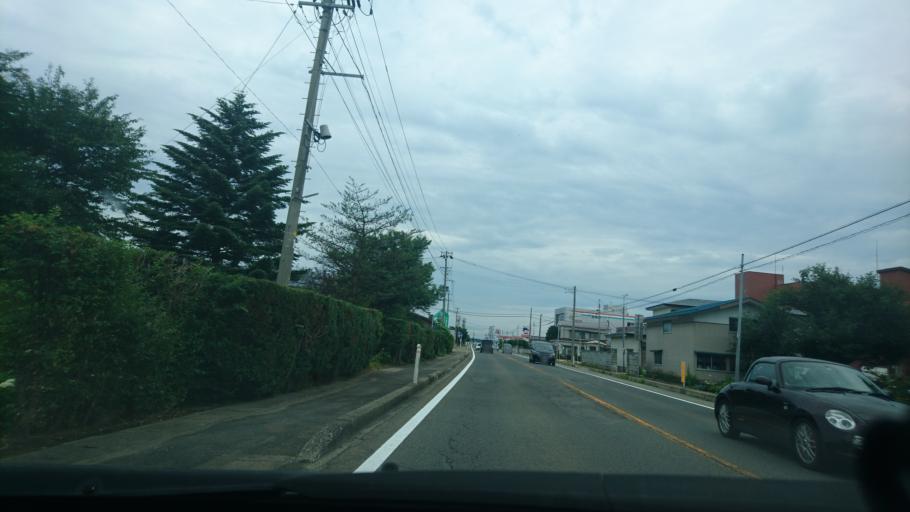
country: JP
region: Akita
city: Yokotemachi
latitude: 39.4011
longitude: 140.5623
